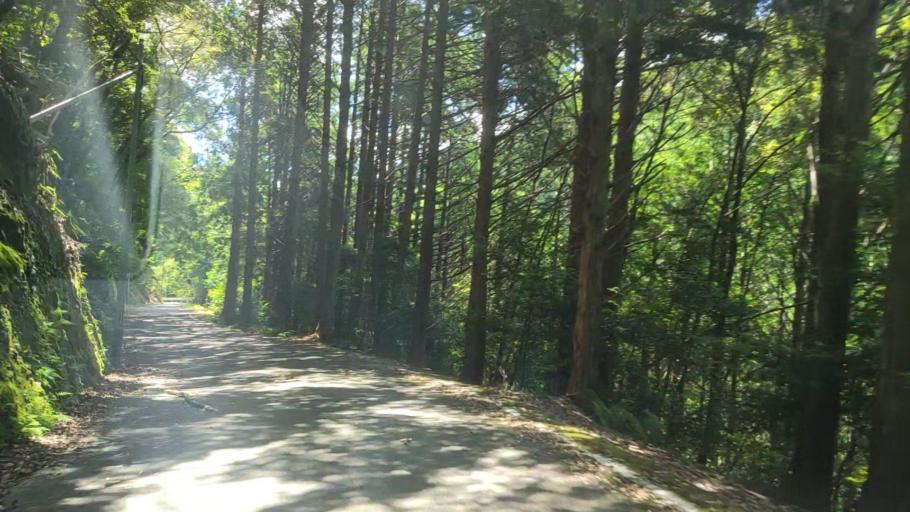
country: JP
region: Wakayama
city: Shingu
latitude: 33.9072
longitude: 135.8660
